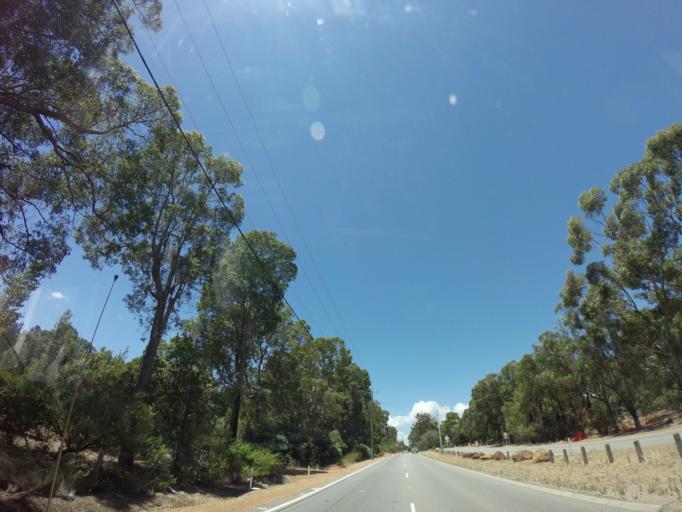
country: AU
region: Western Australia
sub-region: Mundaring
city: Mundaring
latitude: -31.9010
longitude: 116.1532
